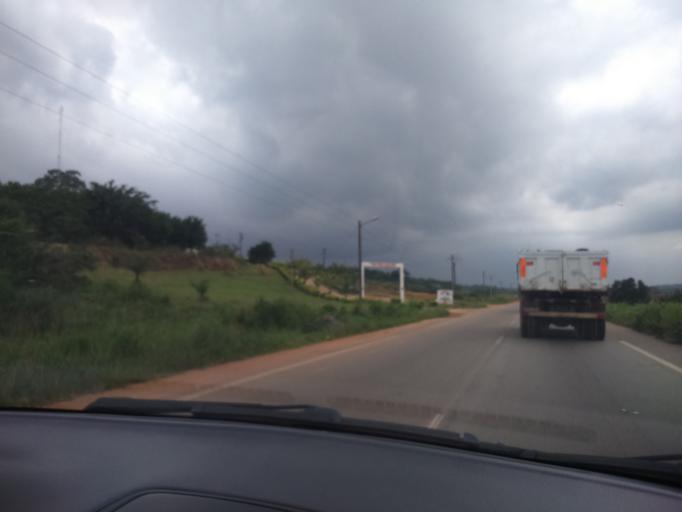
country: CI
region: Lagunes
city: Anyama
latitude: 5.5083
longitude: -4.0620
